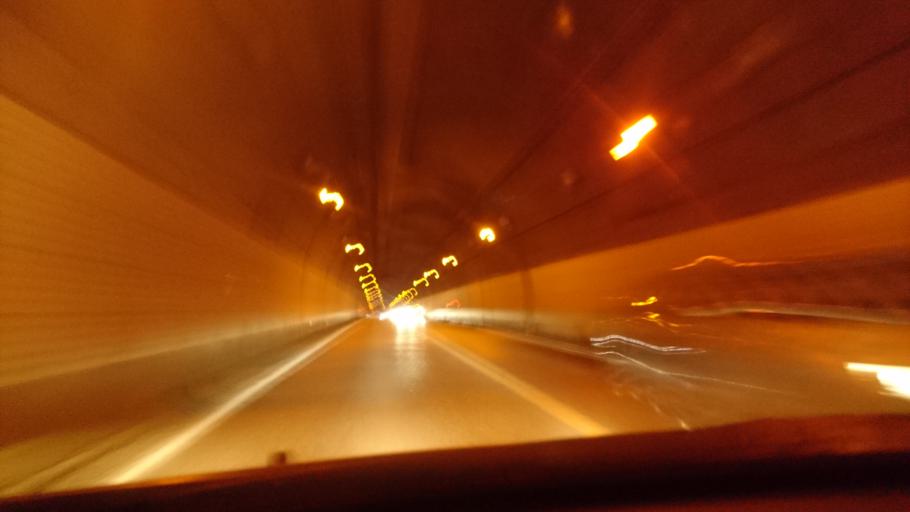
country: JP
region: Iwate
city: Kamaishi
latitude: 39.2224
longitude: 141.8757
